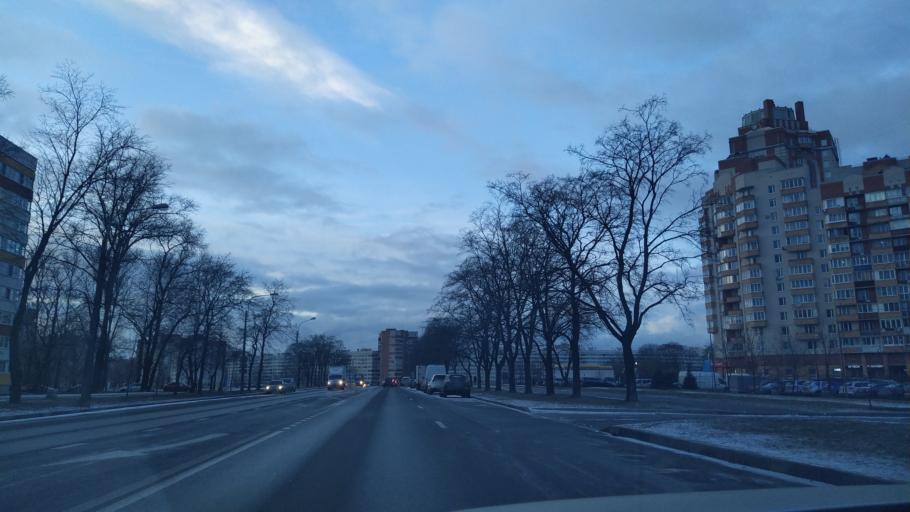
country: RU
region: St.-Petersburg
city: Dachnoye
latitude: 59.8495
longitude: 30.2409
